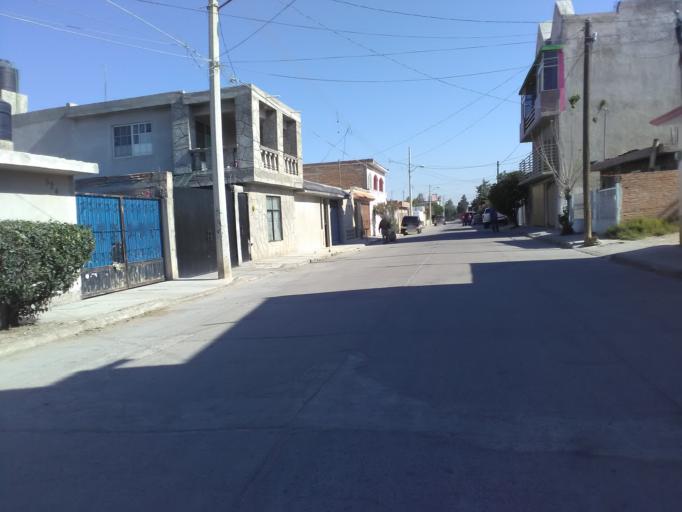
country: MX
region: Durango
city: Victoria de Durango
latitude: 24.0116
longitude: -104.6392
